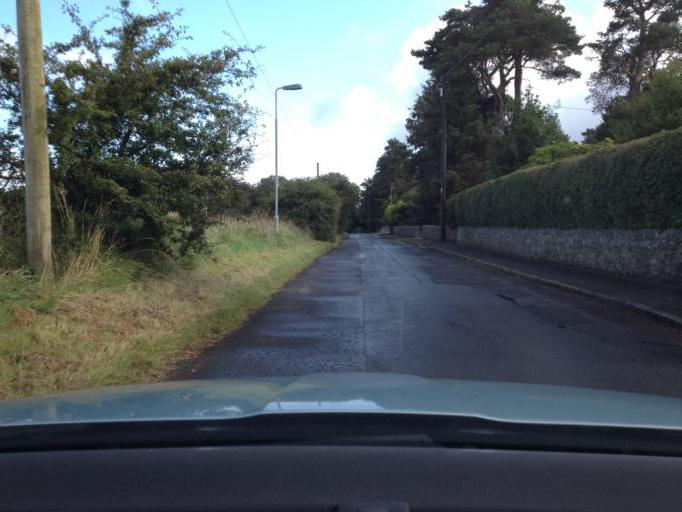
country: GB
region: Scotland
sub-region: West Lothian
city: West Calder
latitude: 55.8375
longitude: -3.5333
